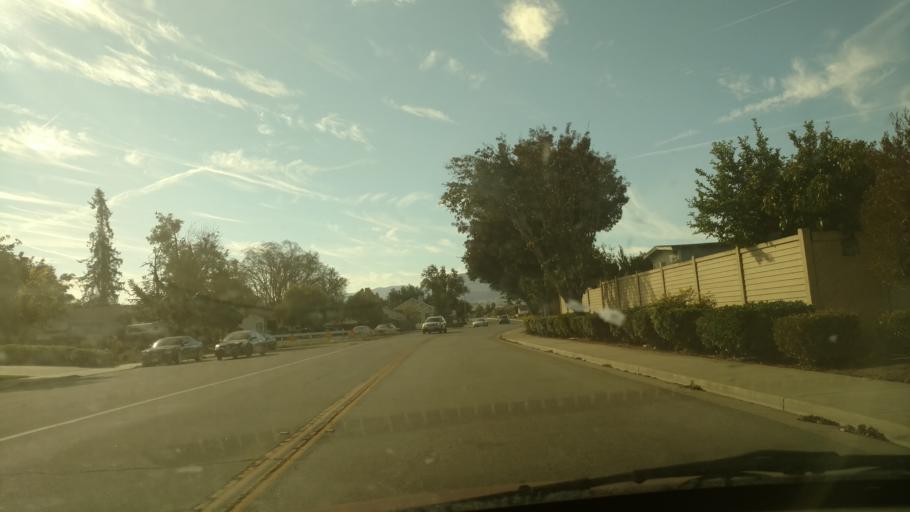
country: US
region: California
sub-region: San Benito County
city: Hollister
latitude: 36.8501
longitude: -121.4141
